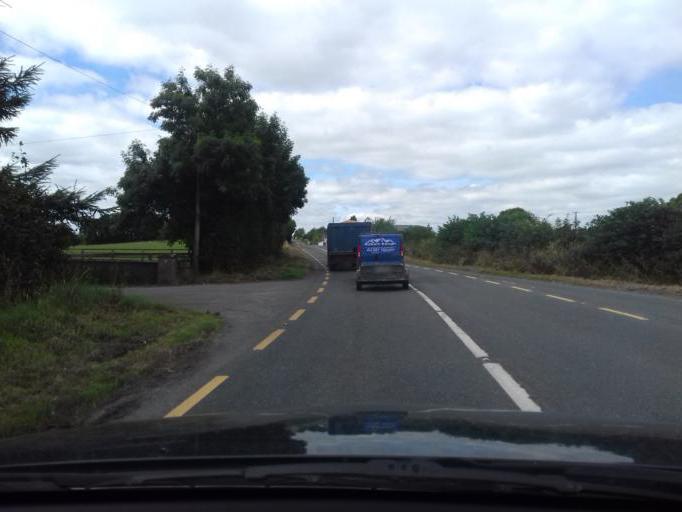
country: IE
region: Leinster
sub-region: Wicklow
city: Baltinglass
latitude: 52.9153
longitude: -6.7023
